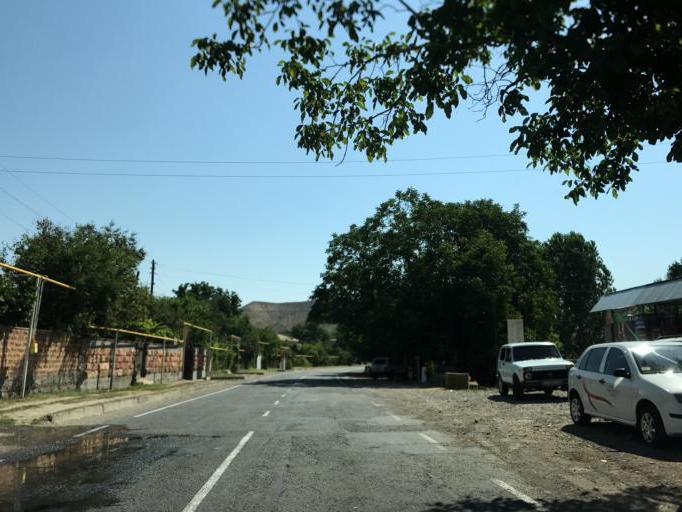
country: AM
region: Vayots' Dzori Marz
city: Getap'
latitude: 39.7383
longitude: 45.2588
